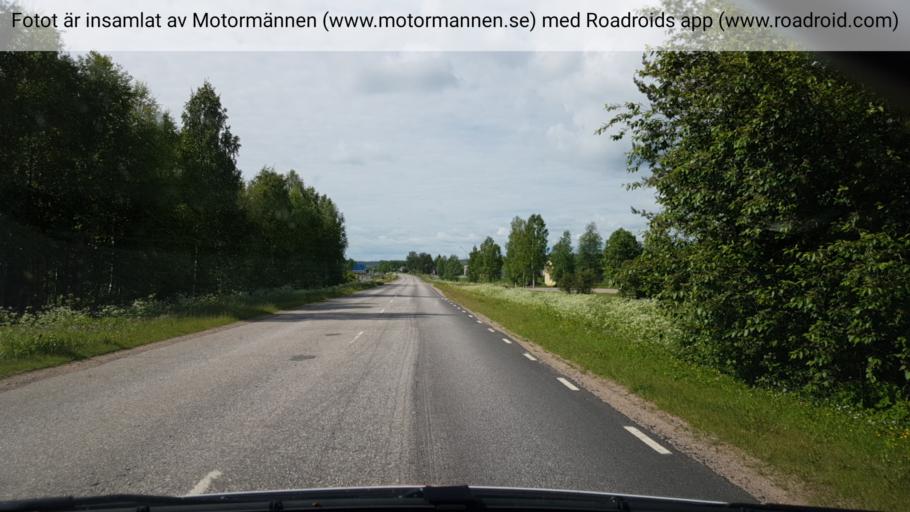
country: FI
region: Lapland
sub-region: Torniolaakso
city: Pello
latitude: 66.5620
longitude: 23.8406
